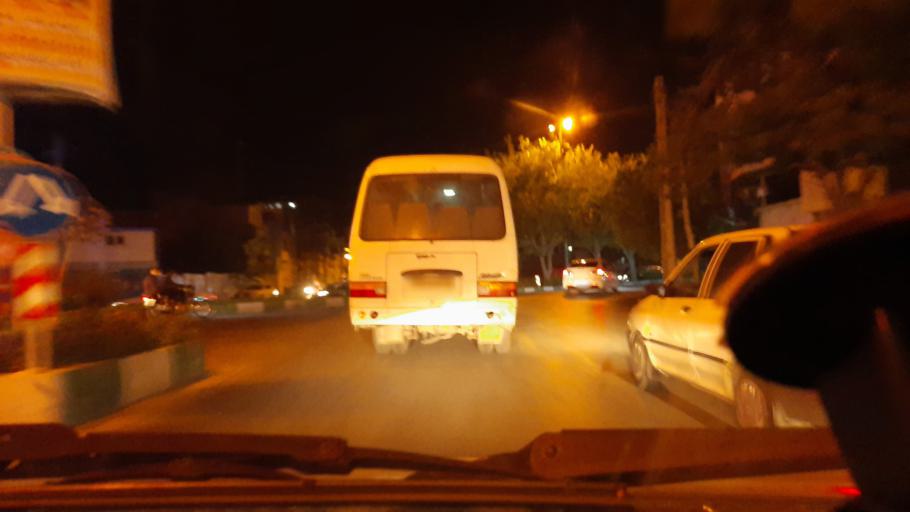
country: IR
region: Markazi
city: Arak
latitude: 34.0780
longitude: 49.6963
